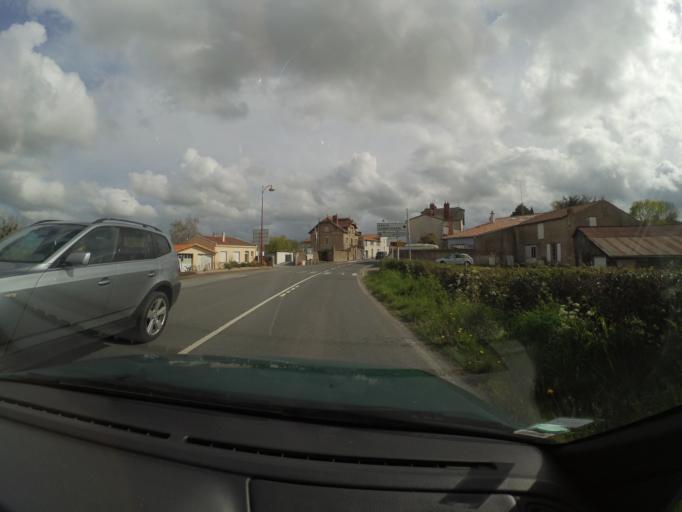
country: FR
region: Pays de la Loire
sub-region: Departement de Maine-et-Loire
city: Lire
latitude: 47.3465
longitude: -1.1632
